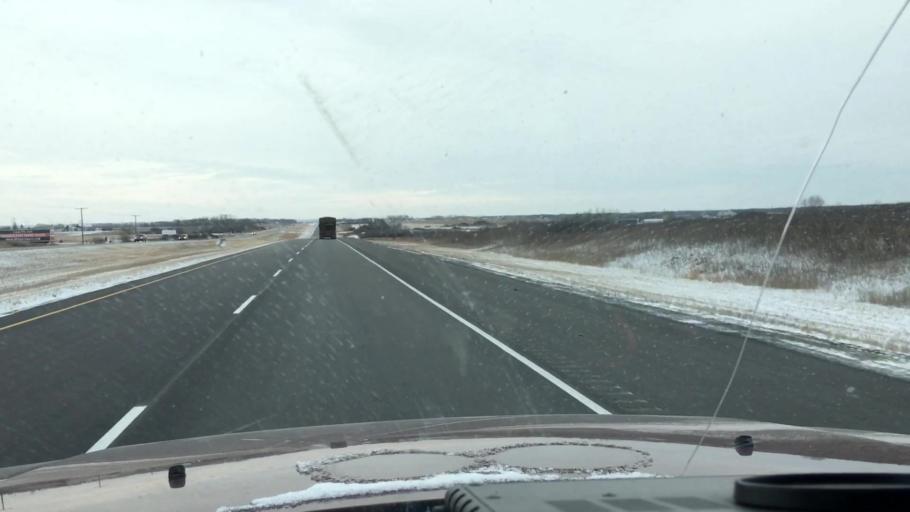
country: CA
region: Saskatchewan
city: Saskatoon
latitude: 51.9268
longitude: -106.5339
